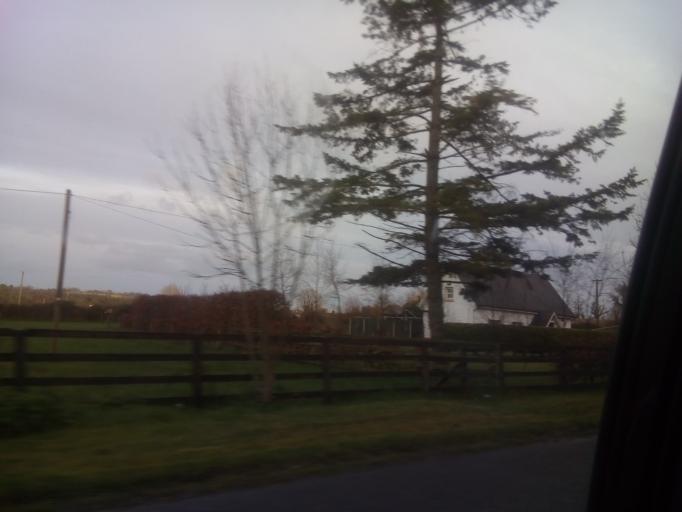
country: IE
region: Leinster
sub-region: Laois
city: Abbeyleix
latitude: 52.8833
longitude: -7.3643
